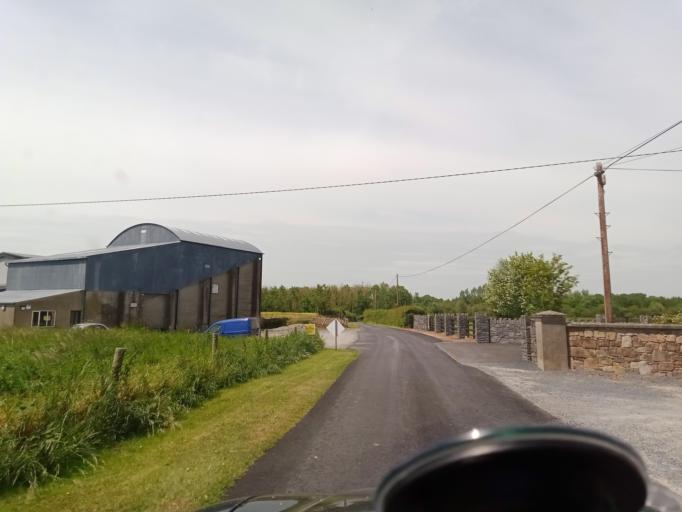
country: IE
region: Leinster
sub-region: Kilkenny
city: Thomastown
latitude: 52.5579
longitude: -7.1126
